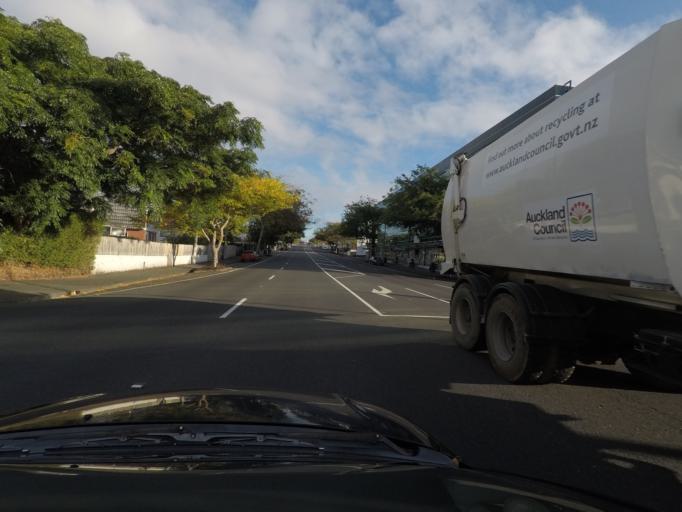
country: NZ
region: Auckland
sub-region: Auckland
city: Auckland
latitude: -36.8983
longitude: 174.8031
